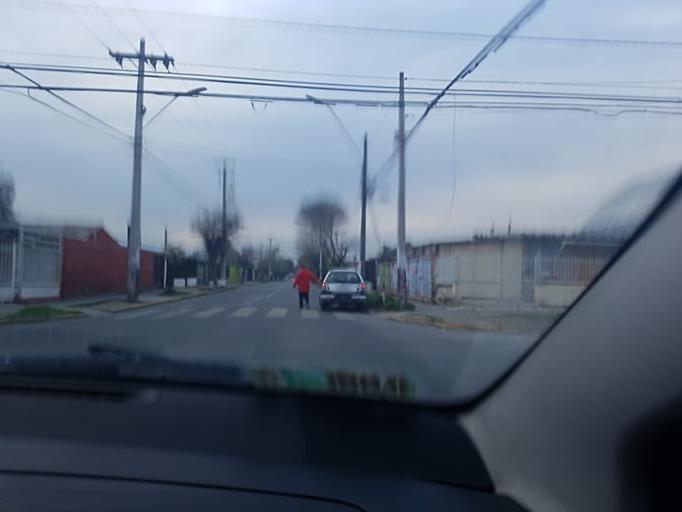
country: CL
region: Santiago Metropolitan
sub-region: Provincia de Santiago
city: Lo Prado
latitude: -33.4738
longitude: -70.6994
